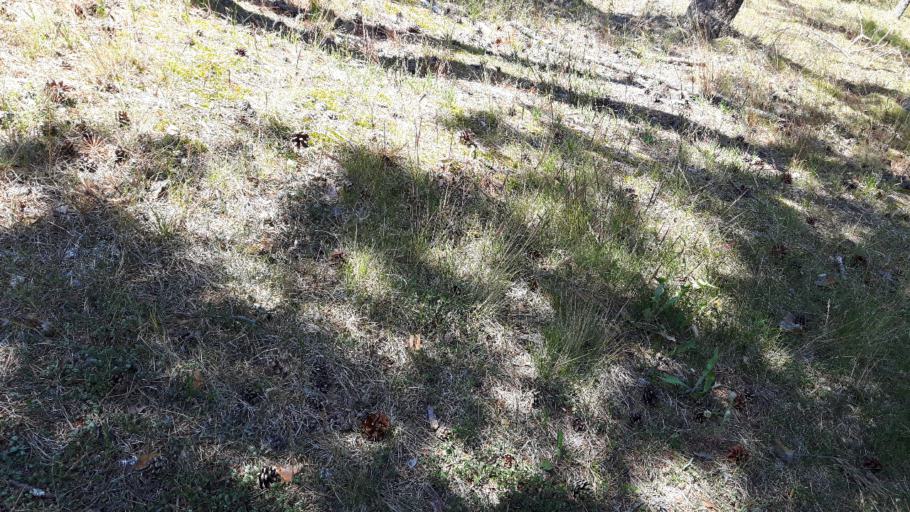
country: LT
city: Neringa
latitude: 55.4176
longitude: 21.0782
